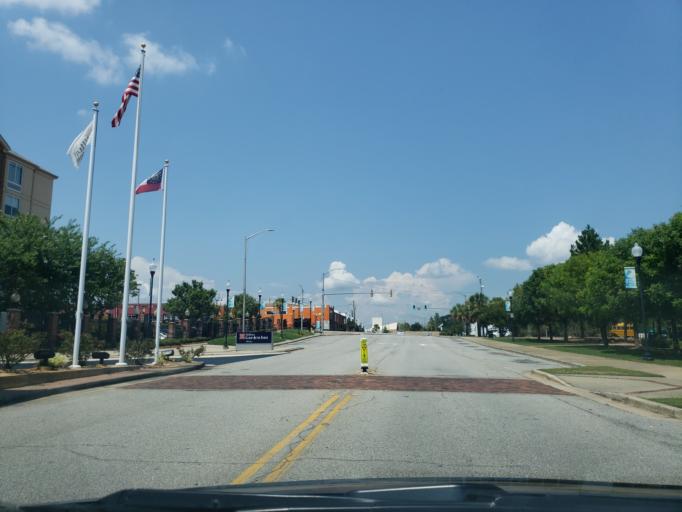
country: US
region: Georgia
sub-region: Dougherty County
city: Albany
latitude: 31.5760
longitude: -84.1490
